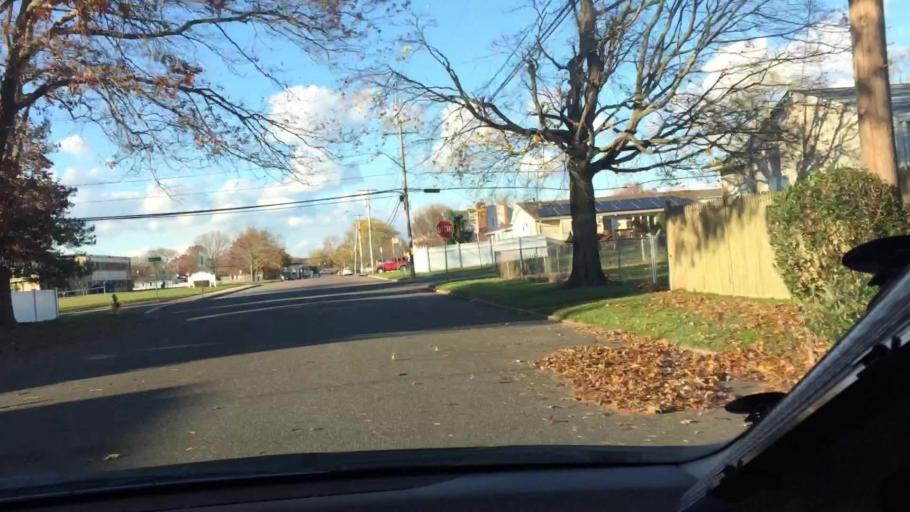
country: US
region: New York
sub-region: Suffolk County
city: Deer Park
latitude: 40.7508
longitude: -73.3348
